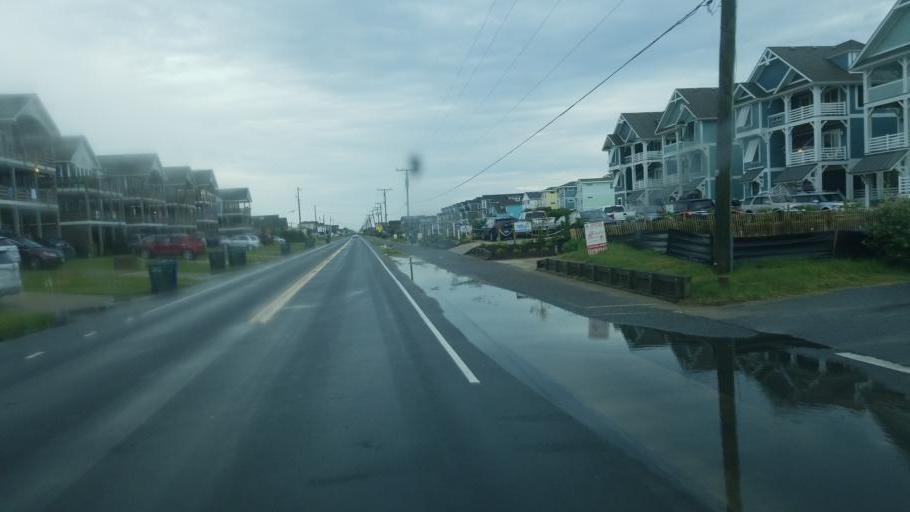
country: US
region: North Carolina
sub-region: Dare County
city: Nags Head
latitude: 35.9835
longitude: -75.6390
